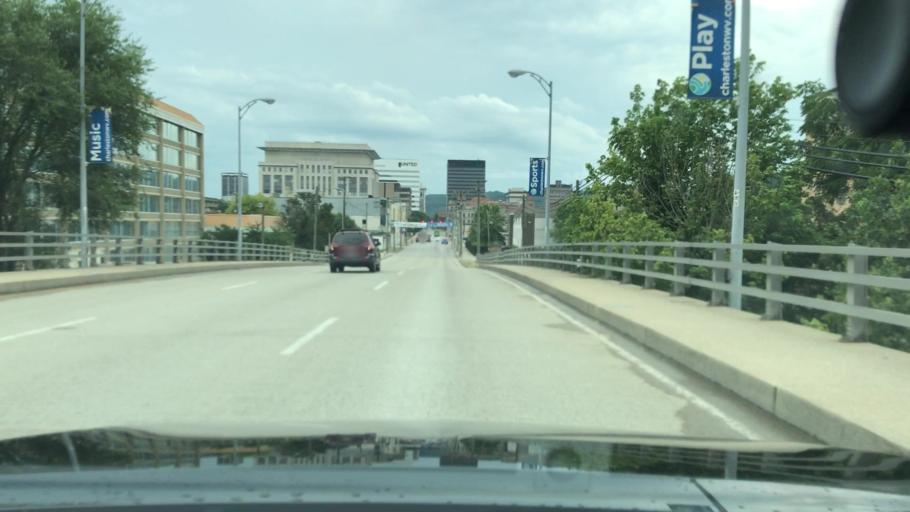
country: US
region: West Virginia
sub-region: Kanawha County
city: Charleston
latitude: 38.3555
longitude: -81.6436
